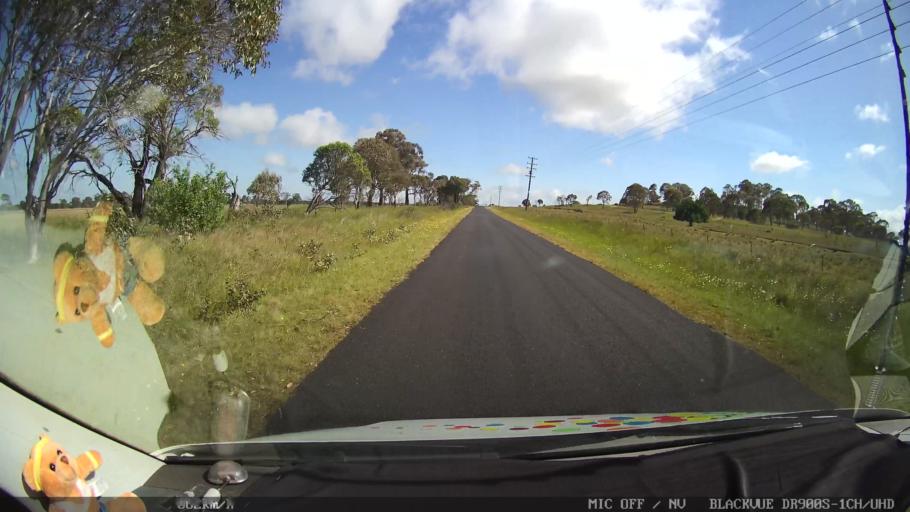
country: AU
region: New South Wales
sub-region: Guyra
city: Guyra
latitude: -30.1987
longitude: 151.6754
